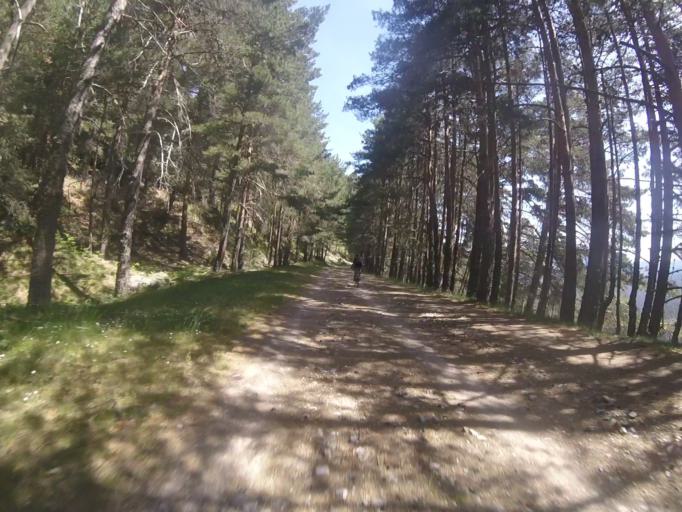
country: ES
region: Madrid
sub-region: Provincia de Madrid
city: Cercedilla
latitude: 40.7980
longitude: -4.0617
